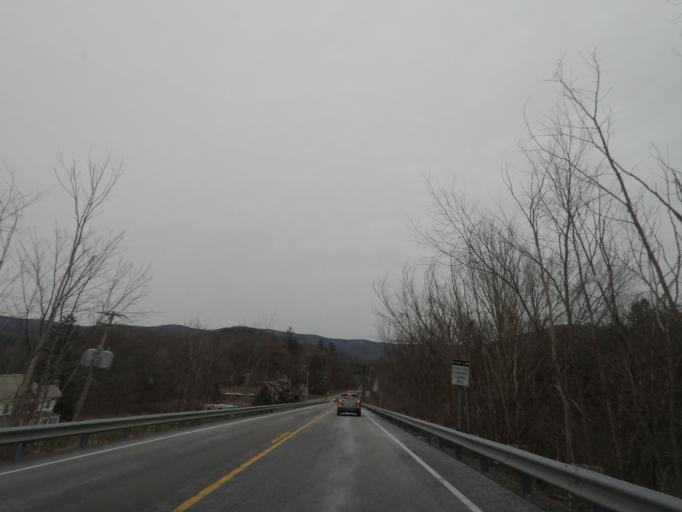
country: US
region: Massachusetts
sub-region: Berkshire County
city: Williamstown
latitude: 42.7511
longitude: -73.3454
